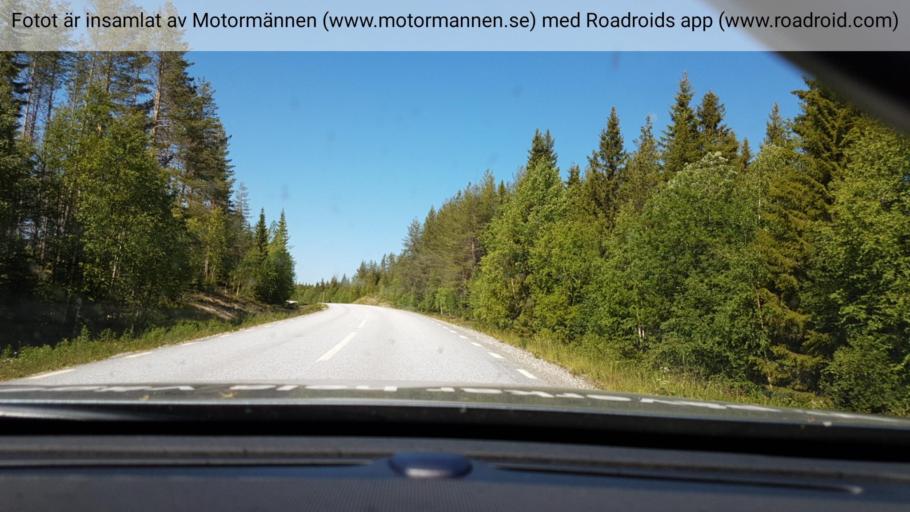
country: SE
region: Vaesterbotten
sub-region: Vilhelmina Kommun
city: Sjoberg
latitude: 64.8249
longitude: 15.9593
